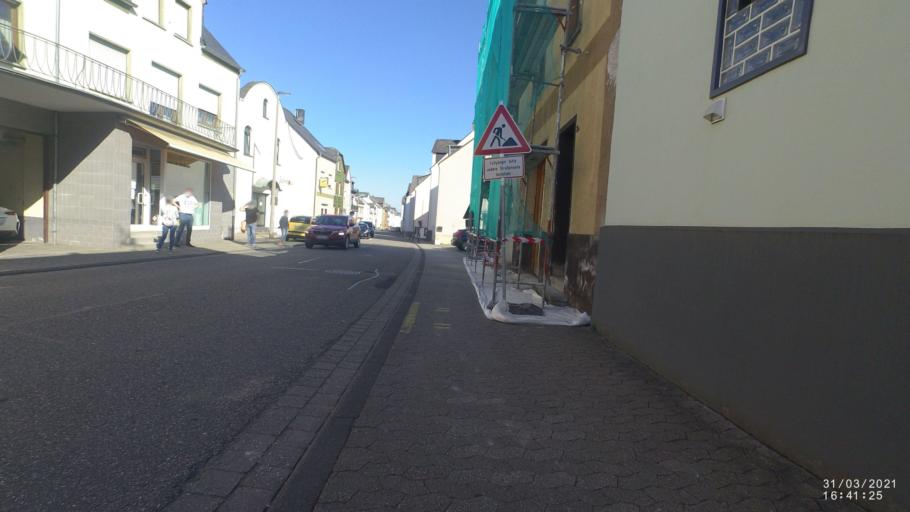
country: DE
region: Rheinland-Pfalz
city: Mulheim-Karlich
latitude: 50.3883
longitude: 7.5035
